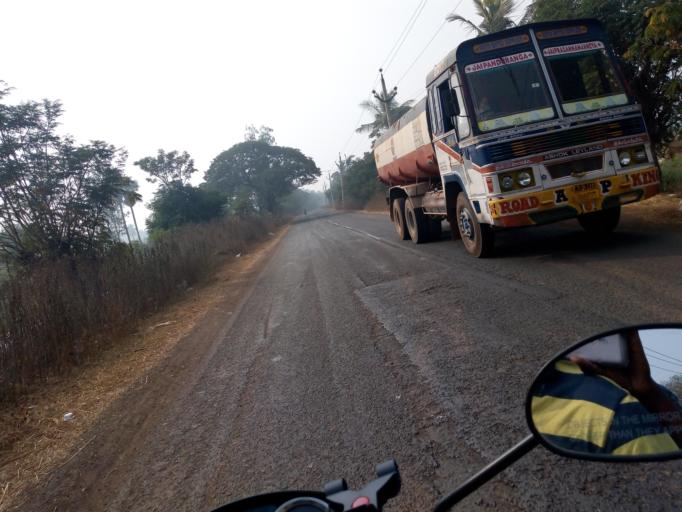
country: IN
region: Andhra Pradesh
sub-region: West Godavari
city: Tadepallegudem
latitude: 16.7574
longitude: 81.4237
